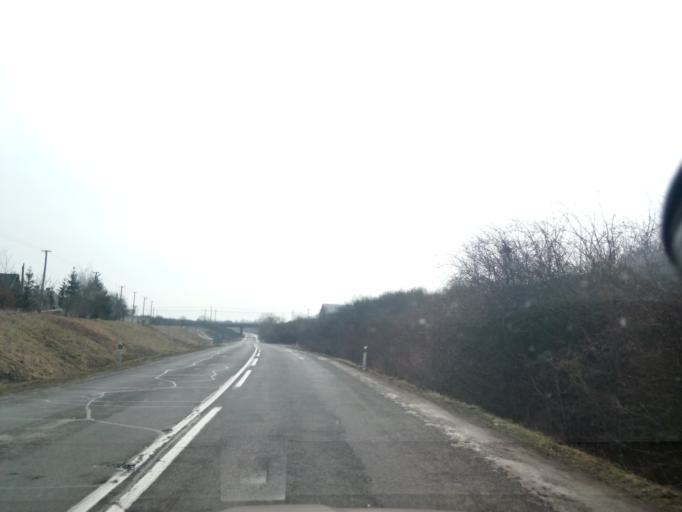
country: SK
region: Kosicky
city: Secovce
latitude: 48.6228
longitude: 21.5897
